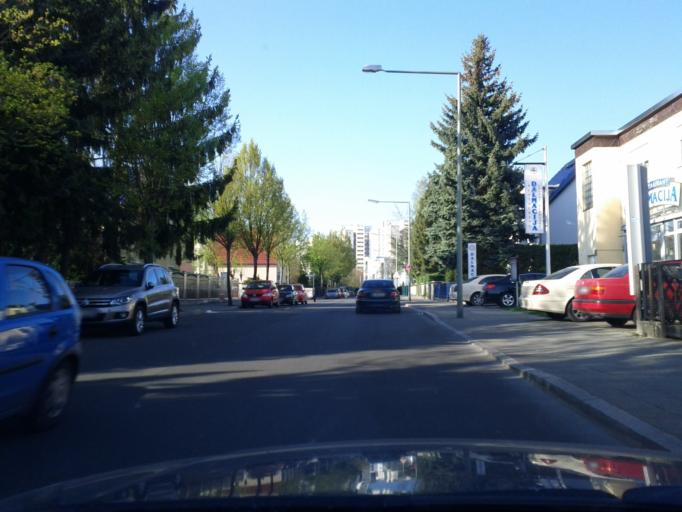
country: DE
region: Berlin
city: Markisches Viertel
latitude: 52.5938
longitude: 13.3471
